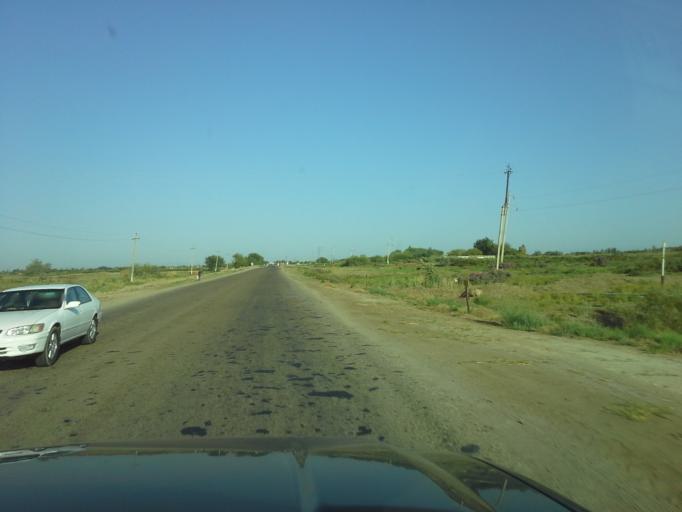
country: UZ
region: Karakalpakstan
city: Khujayli
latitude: 42.2281
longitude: 59.4713
